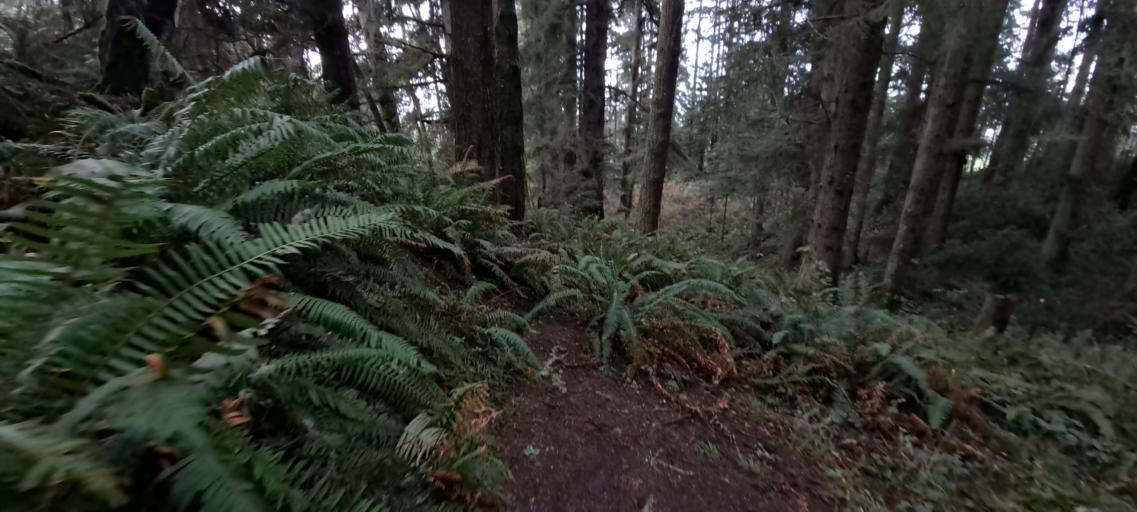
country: US
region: California
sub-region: Humboldt County
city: Ferndale
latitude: 40.5693
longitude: -124.2568
